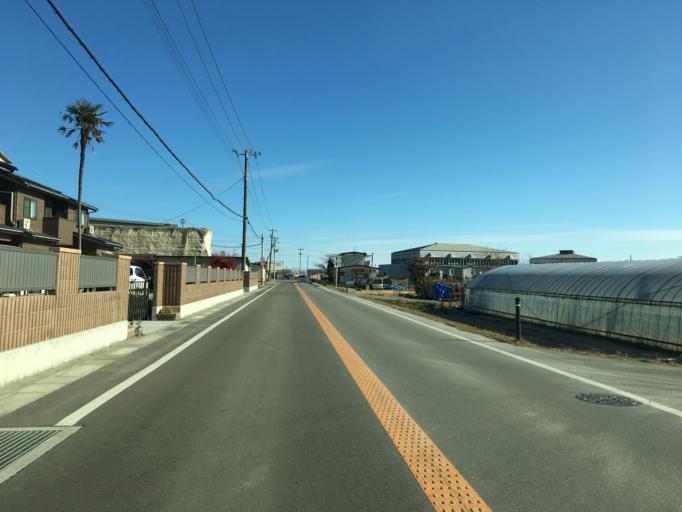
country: JP
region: Miyagi
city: Marumori
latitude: 37.8046
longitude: 140.9649
